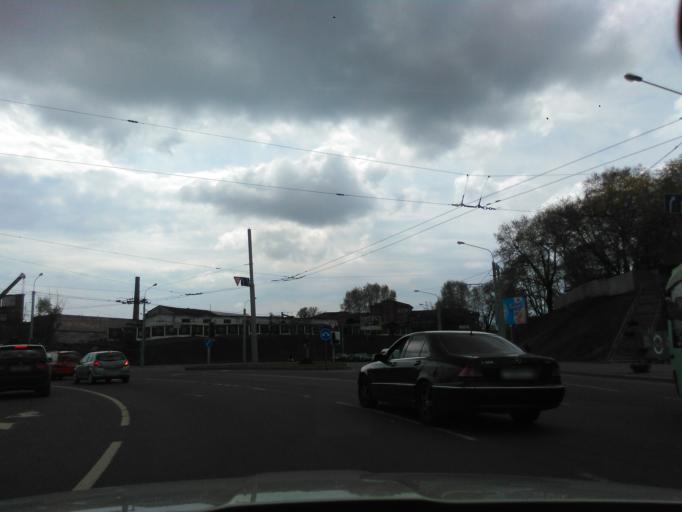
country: BY
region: Minsk
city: Minsk
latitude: 53.8966
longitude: 27.5373
